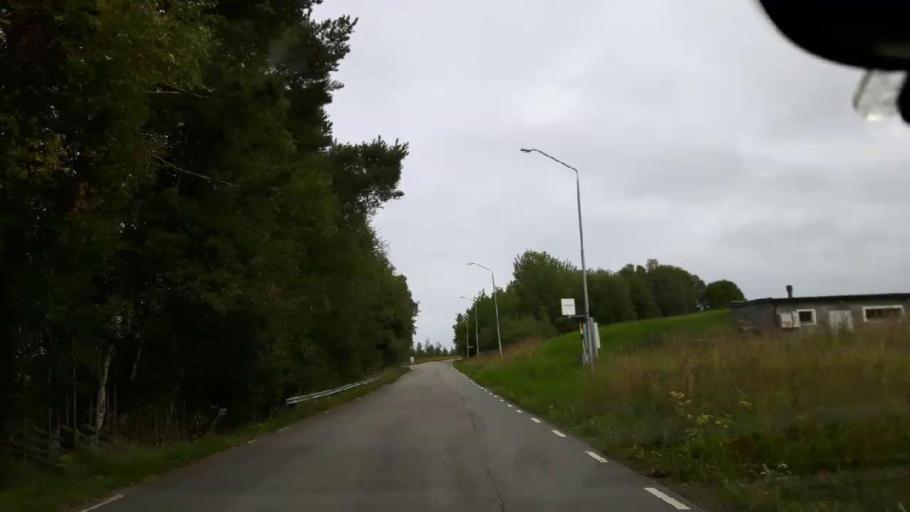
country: SE
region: Jaemtland
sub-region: OEstersunds Kommun
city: Ostersund
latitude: 63.1754
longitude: 14.5166
